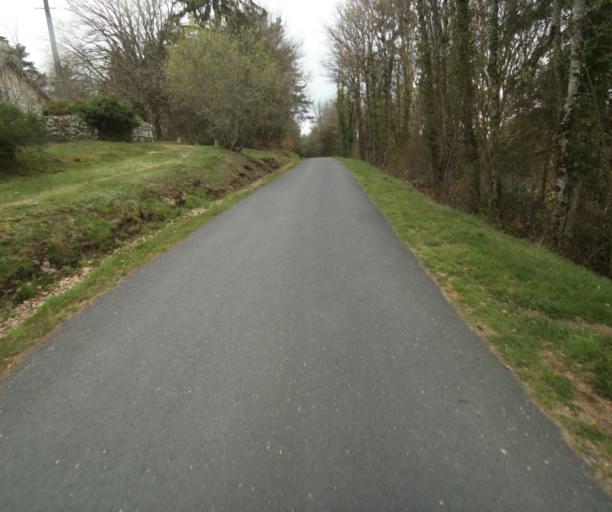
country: FR
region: Limousin
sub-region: Departement de la Correze
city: Correze
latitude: 45.3044
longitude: 1.9086
